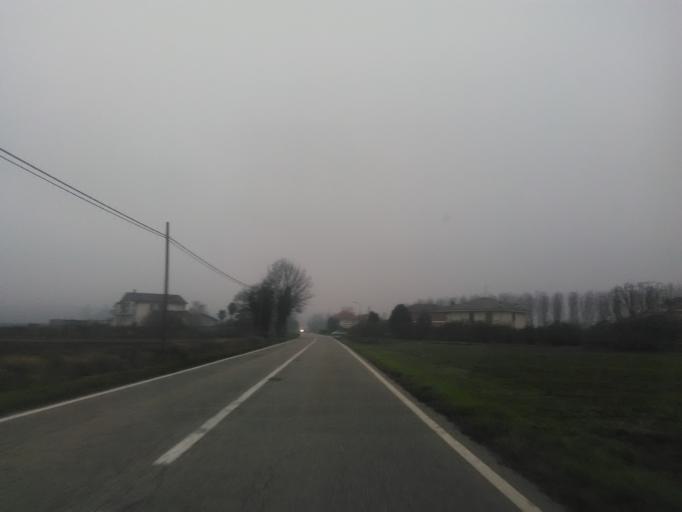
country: IT
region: Piedmont
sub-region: Provincia di Vercelli
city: Moncrivello
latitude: 45.3232
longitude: 8.0119
